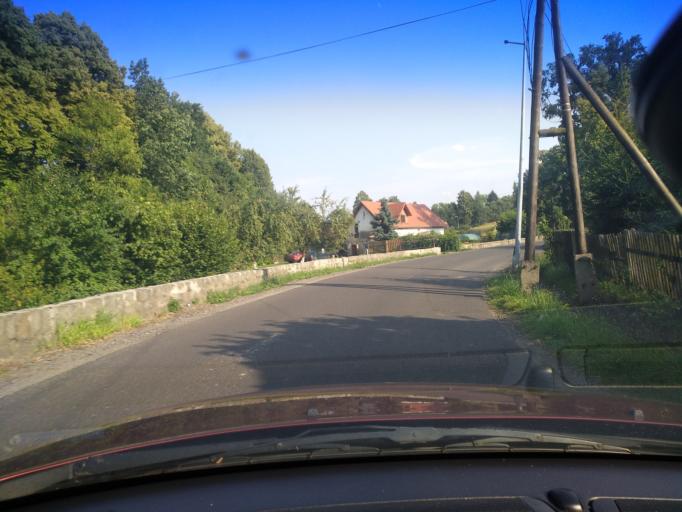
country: PL
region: Lower Silesian Voivodeship
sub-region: Powiat lubanski
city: Siekierczyn
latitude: 51.0696
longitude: 15.1648
